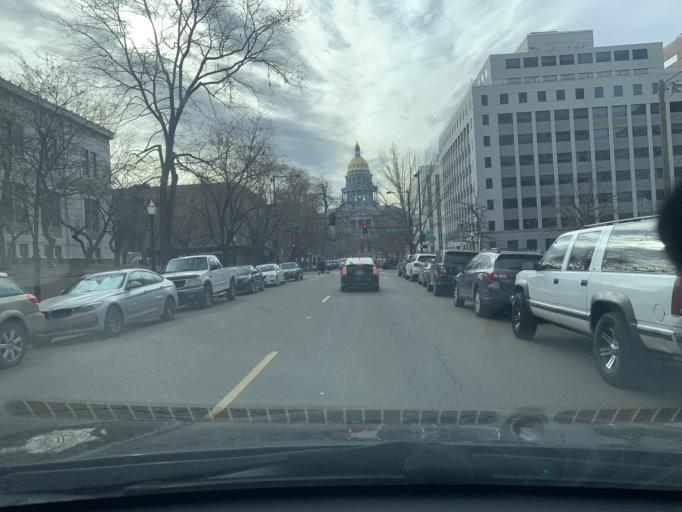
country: US
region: Colorado
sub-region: Denver County
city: Denver
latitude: 39.7423
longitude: -104.9849
